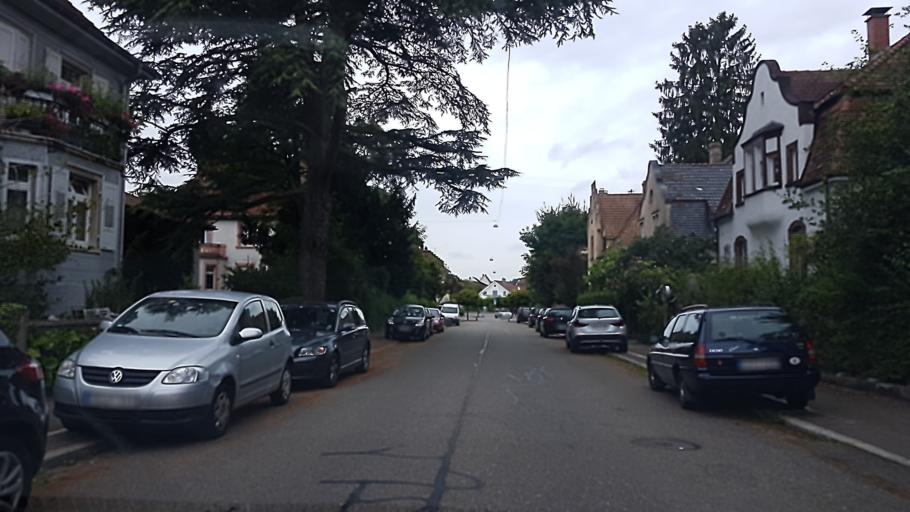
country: DE
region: Baden-Wuerttemberg
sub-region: Freiburg Region
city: Emmendingen
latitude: 48.1180
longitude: 7.8555
